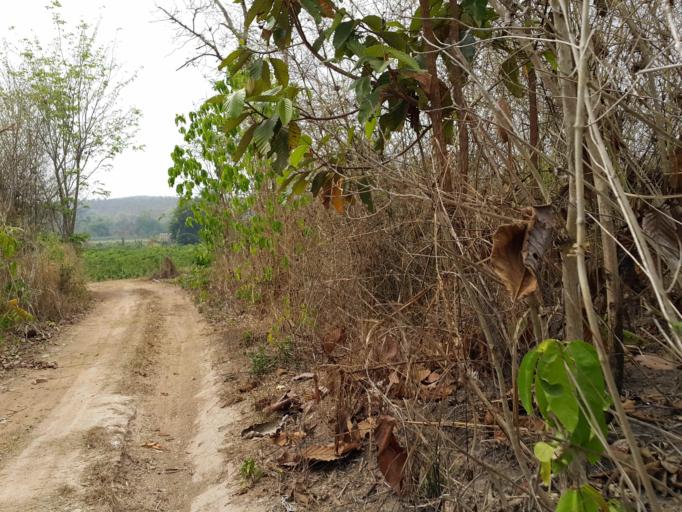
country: TH
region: Chiang Mai
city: Mae Taeng
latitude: 19.1097
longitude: 98.9856
